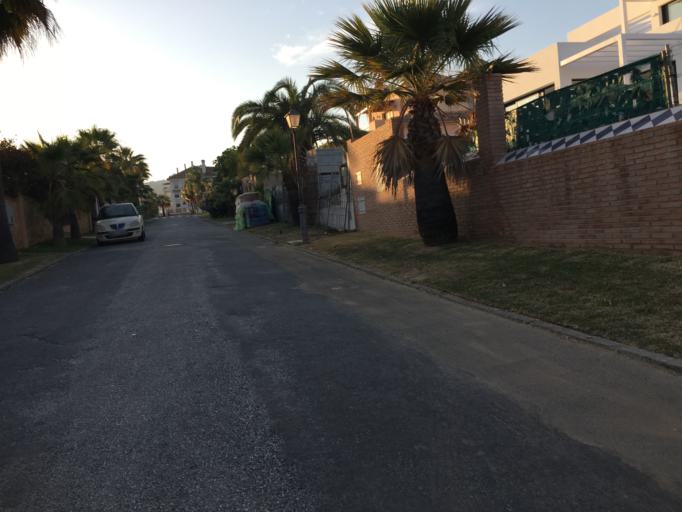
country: ES
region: Andalusia
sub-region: Provincia de Malaga
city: Marbella
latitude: 36.5008
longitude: -4.8132
